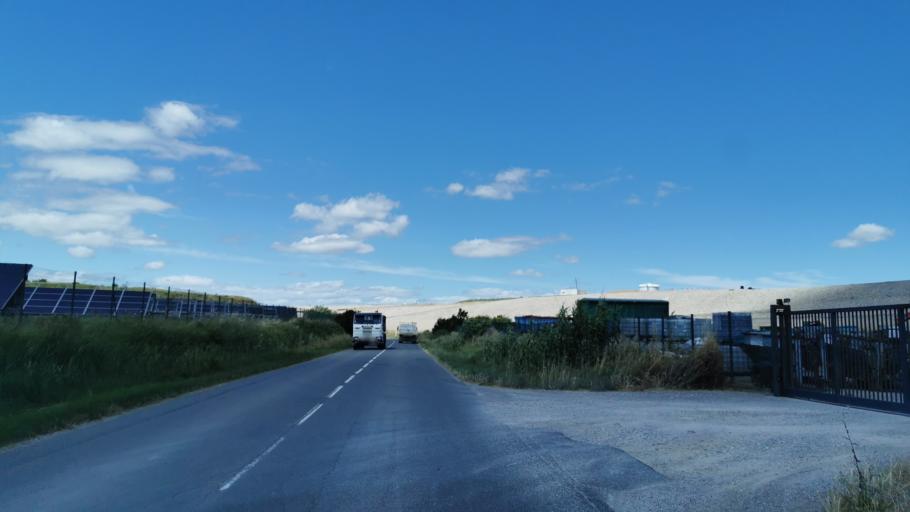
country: FR
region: Languedoc-Roussillon
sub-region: Departement de l'Aude
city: Narbonne
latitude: 43.2084
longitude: 2.9817
